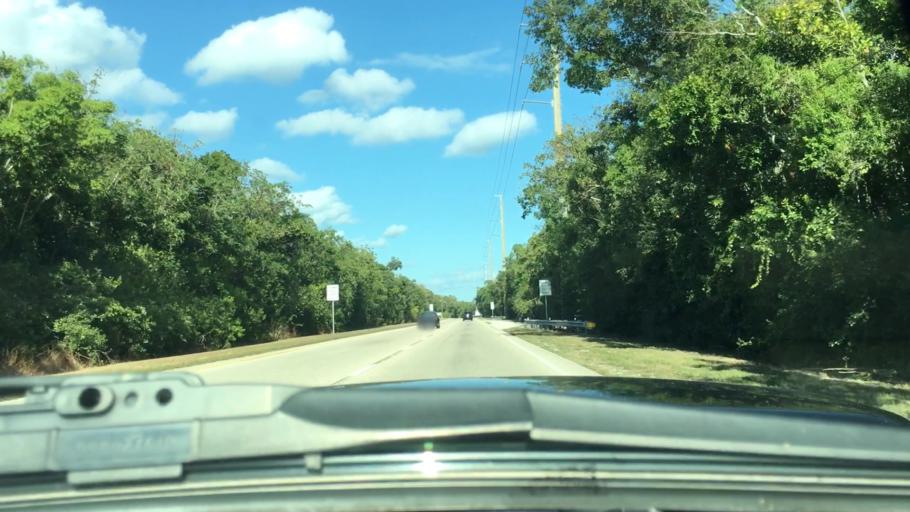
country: US
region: Florida
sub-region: Monroe County
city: Key Largo
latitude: 25.0688
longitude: -80.4677
